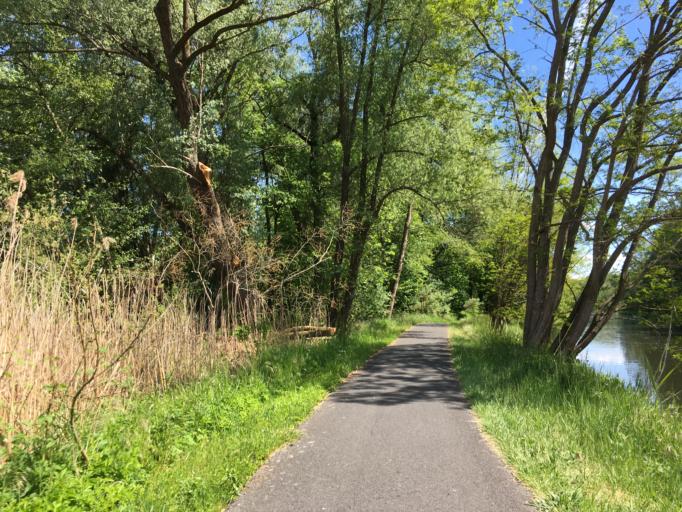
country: DE
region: Brandenburg
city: Eberswalde
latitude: 52.8452
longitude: 13.8405
